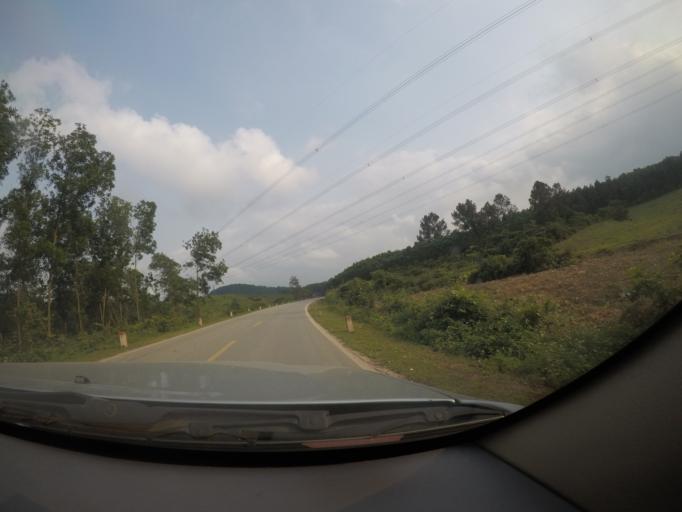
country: VN
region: Quang Binh
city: Kien Giang
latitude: 17.1132
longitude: 106.8353
